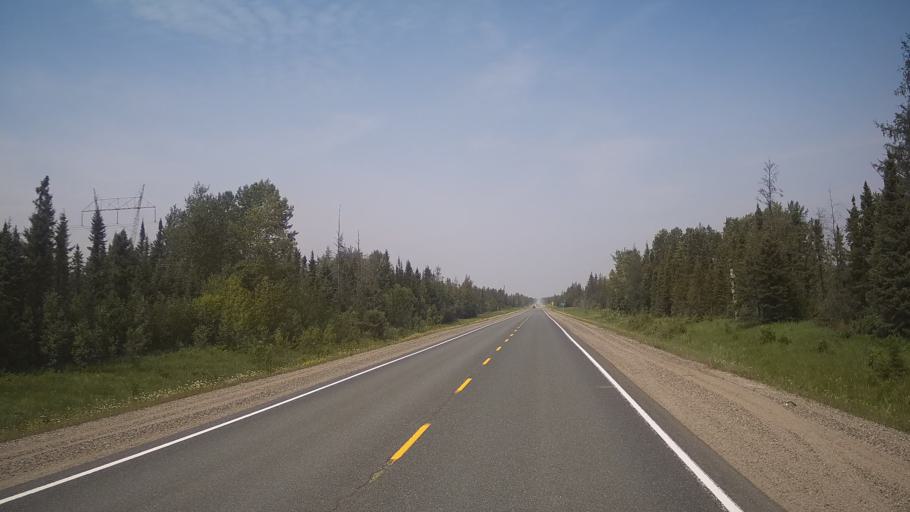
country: CA
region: Ontario
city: Timmins
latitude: 48.7801
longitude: -81.3642
